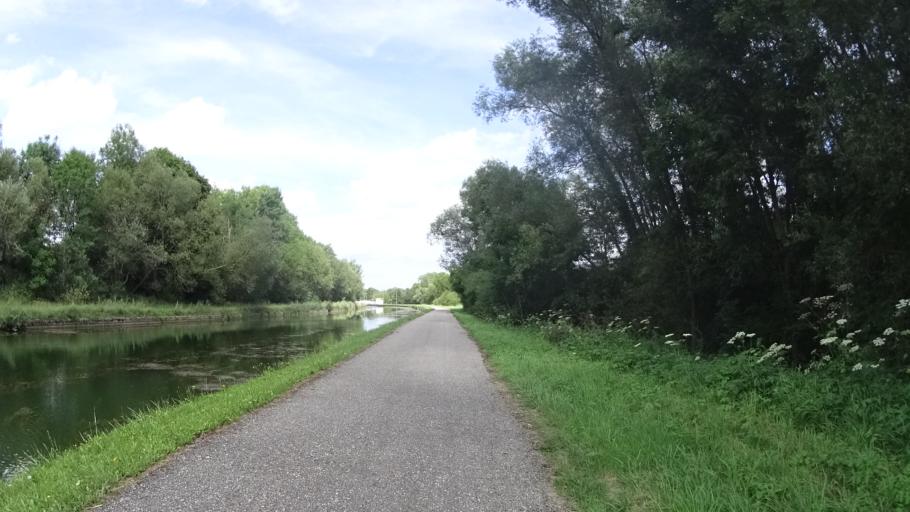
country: FR
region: Lorraine
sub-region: Departement de Meurthe-et-Moselle
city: Ecrouves
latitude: 48.6743
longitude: 5.8591
